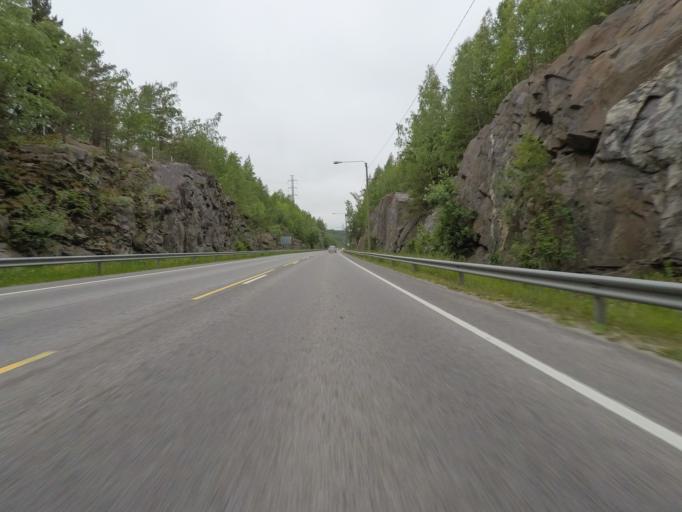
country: FI
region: Varsinais-Suomi
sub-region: Turku
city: Raisio
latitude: 60.4628
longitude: 22.1440
